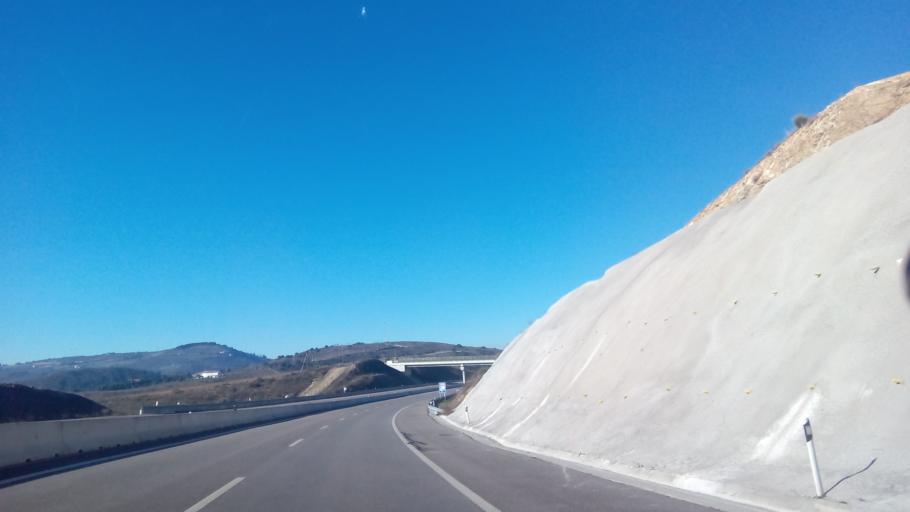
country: PT
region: Braganca
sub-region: Braganca Municipality
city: Braganca
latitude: 41.7821
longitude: -6.7033
